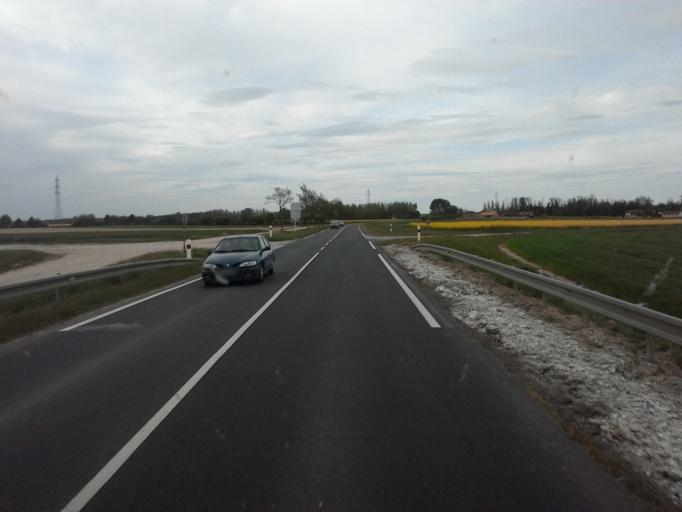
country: FR
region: Champagne-Ardenne
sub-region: Departement de la Marne
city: Saint-Memmie
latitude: 49.0177
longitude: 4.4107
